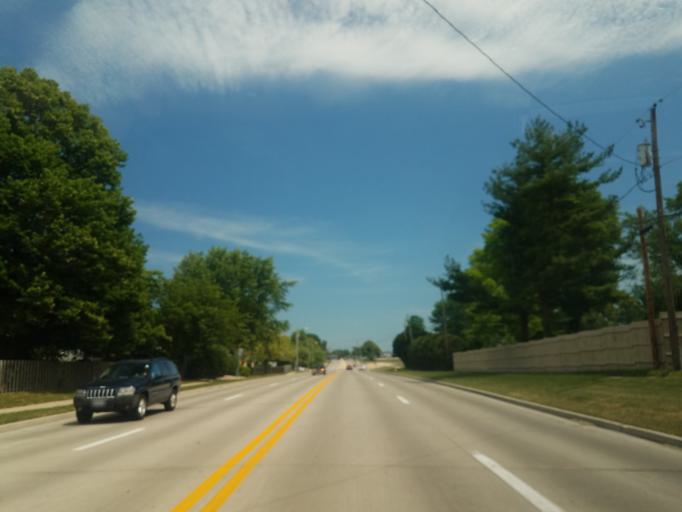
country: US
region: Illinois
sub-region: McLean County
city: Normal
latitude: 40.4974
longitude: -88.9611
